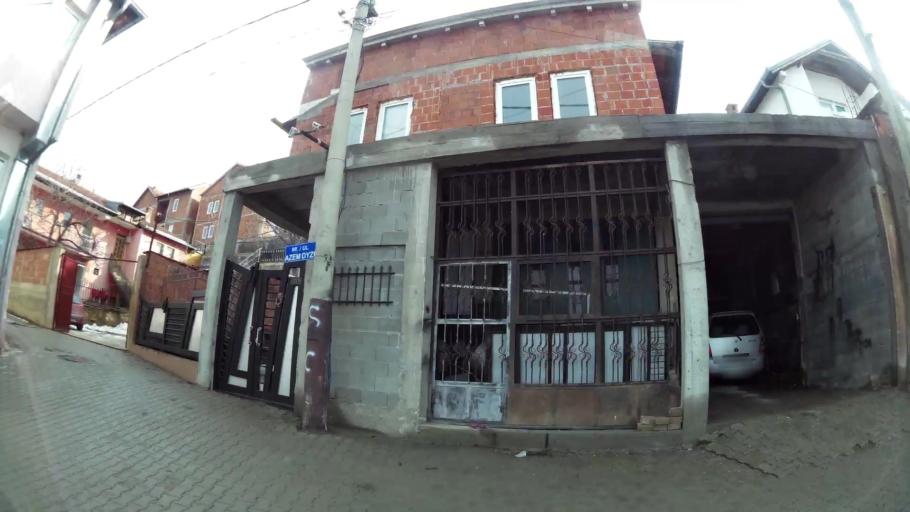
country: XK
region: Pristina
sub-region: Komuna e Prishtines
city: Pristina
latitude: 42.6752
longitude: 21.1760
